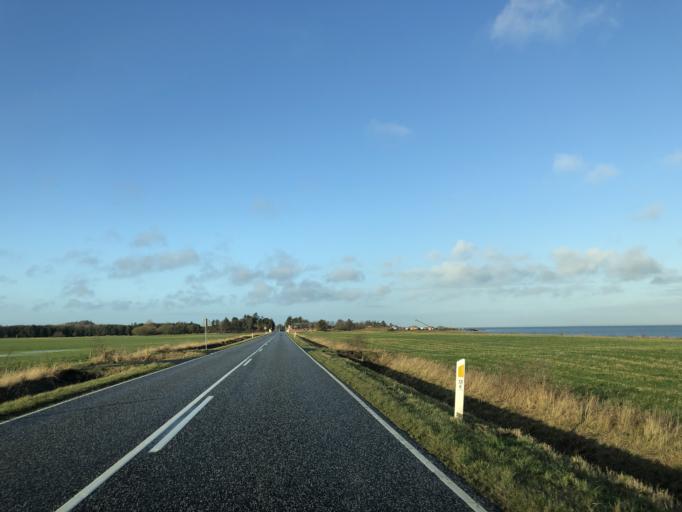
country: DK
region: Central Jutland
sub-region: Struer Kommune
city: Struer
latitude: 56.5426
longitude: 8.5024
